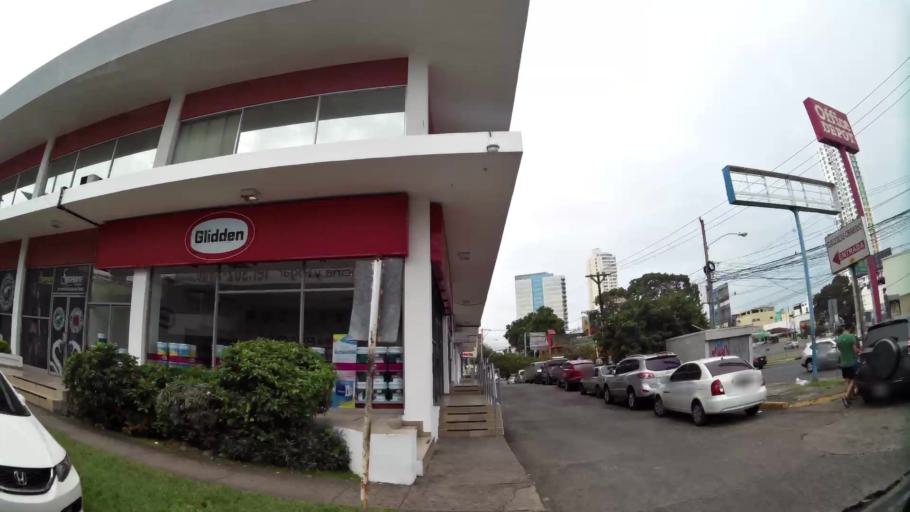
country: PA
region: Panama
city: Panama
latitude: 8.9910
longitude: -79.5204
